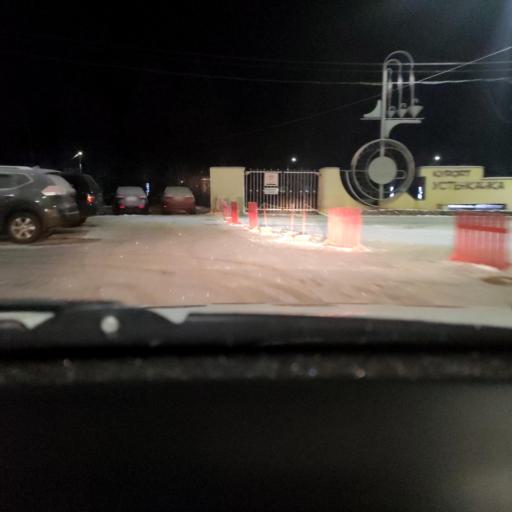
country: RU
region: Perm
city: Ust'-Kachka
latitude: 58.0059
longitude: 55.6700
